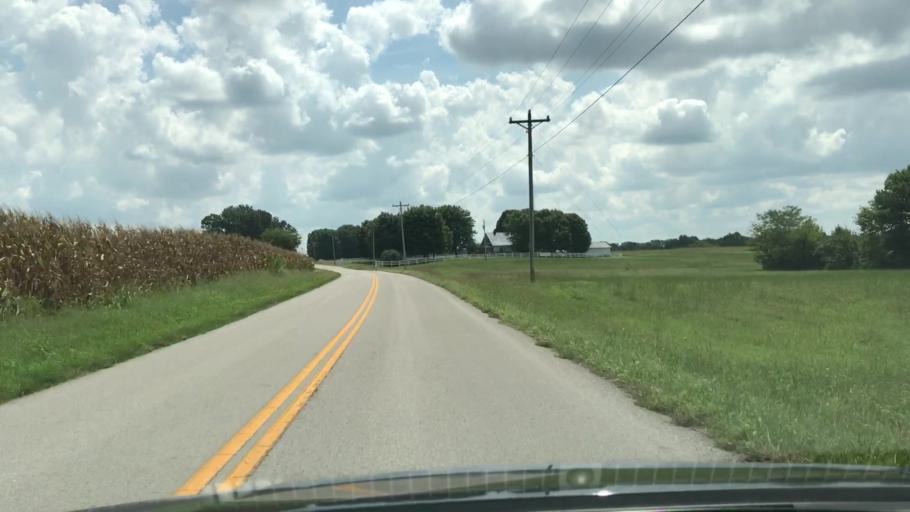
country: US
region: Kentucky
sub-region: Todd County
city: Elkton
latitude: 36.7893
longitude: -87.1356
